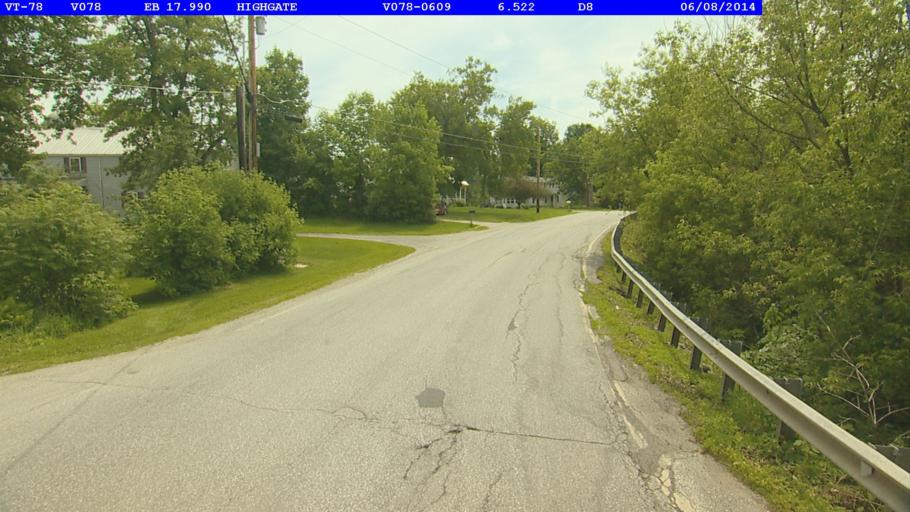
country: US
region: Vermont
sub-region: Franklin County
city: Swanton
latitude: 44.9302
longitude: -72.9866
